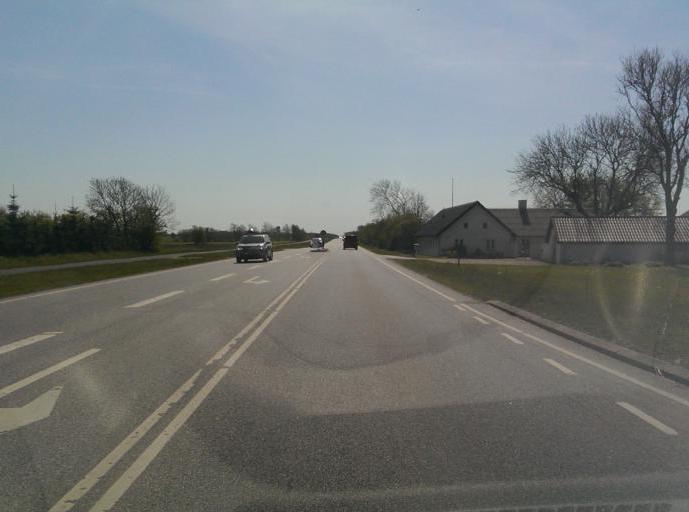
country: DK
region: South Denmark
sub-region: Esbjerg Kommune
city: Ribe
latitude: 55.3832
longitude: 8.7551
